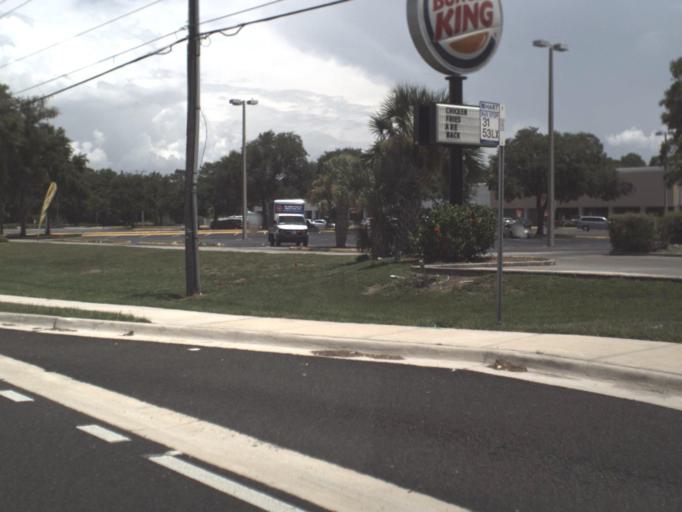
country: US
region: Florida
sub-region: Hillsborough County
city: Riverview
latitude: 27.8578
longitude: -82.3265
